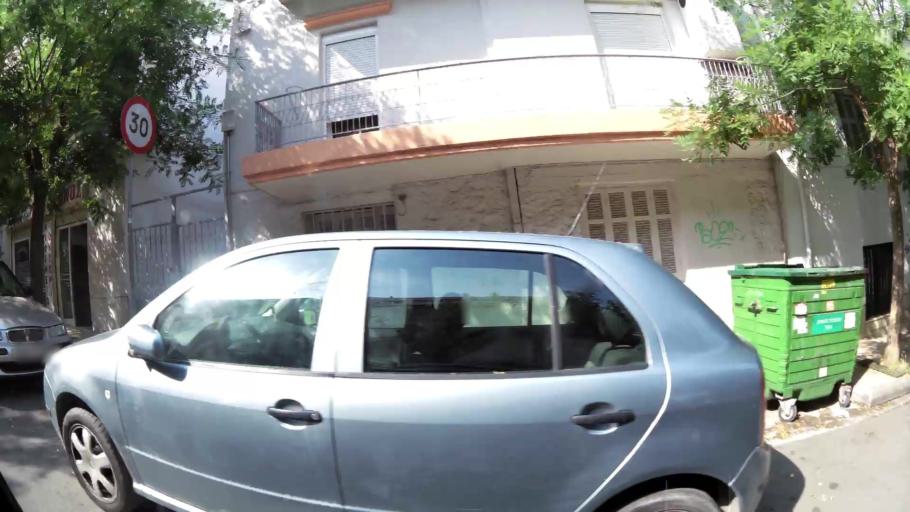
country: GR
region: Central Macedonia
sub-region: Nomos Thessalonikis
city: Sykies
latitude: 40.6485
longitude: 22.9478
